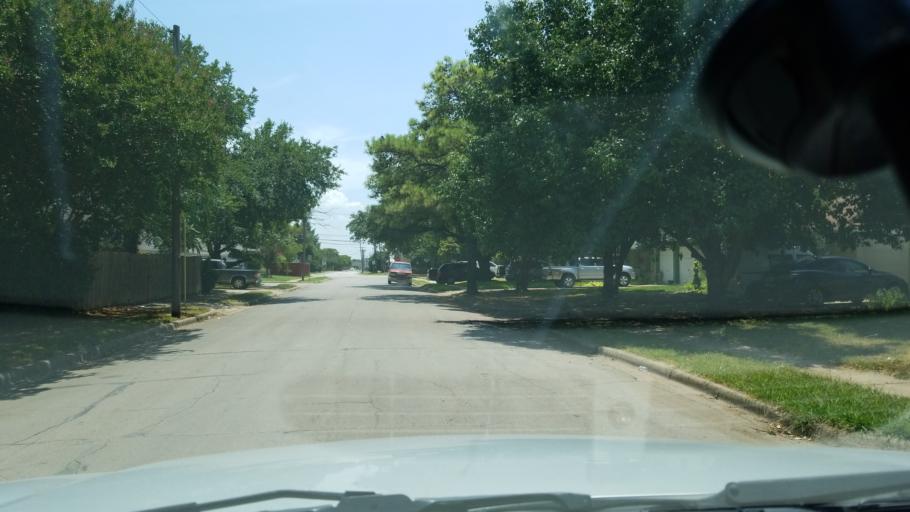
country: US
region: Texas
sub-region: Dallas County
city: Irving
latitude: 32.8229
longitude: -96.9895
